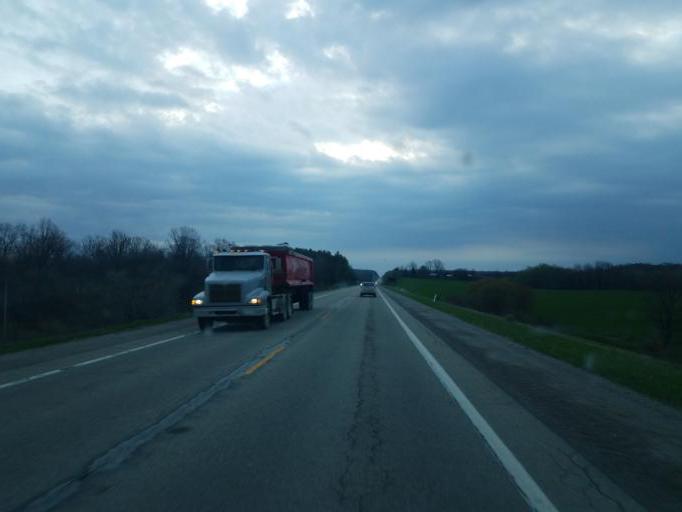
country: US
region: Michigan
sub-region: Isabella County
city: Lake Isabella
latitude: 43.5963
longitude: -85.0014
